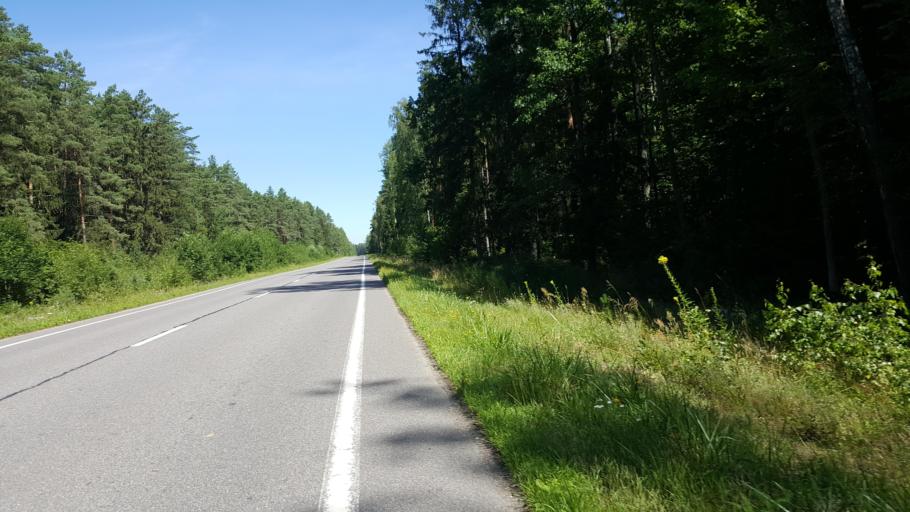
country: BY
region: Brest
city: Pruzhany
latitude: 52.5039
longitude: 24.1761
